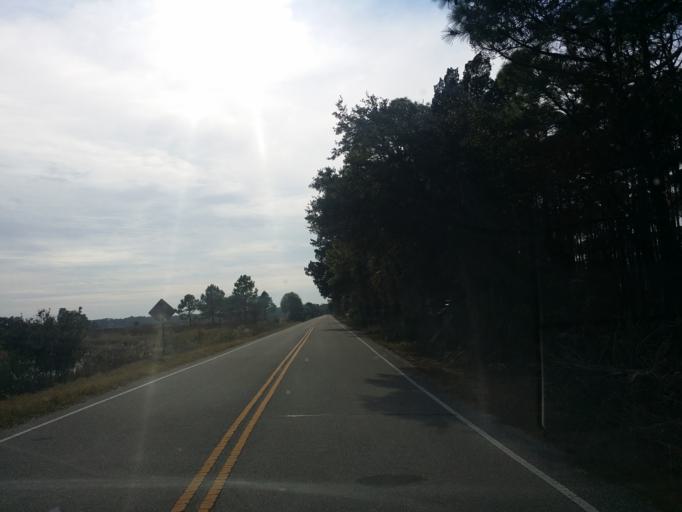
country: US
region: Florida
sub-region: Leon County
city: Woodville
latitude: 30.1109
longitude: -84.1502
